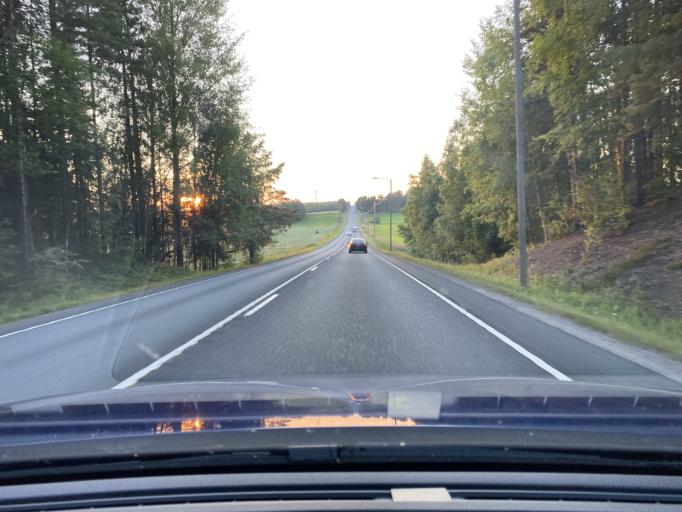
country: FI
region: Pirkanmaa
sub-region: Luoteis-Pirkanmaa
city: Ikaalinen
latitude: 61.7655
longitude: 23.0195
